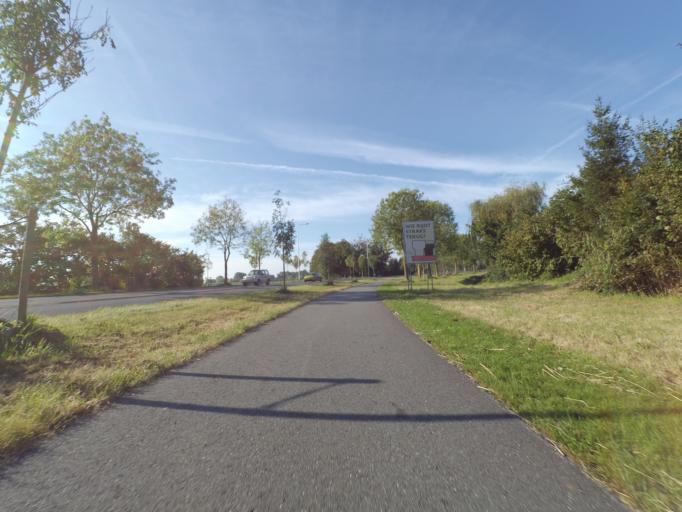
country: NL
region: Gelderland
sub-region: Gemeente Nijkerk
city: Nijkerk
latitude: 52.2092
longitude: 5.4977
